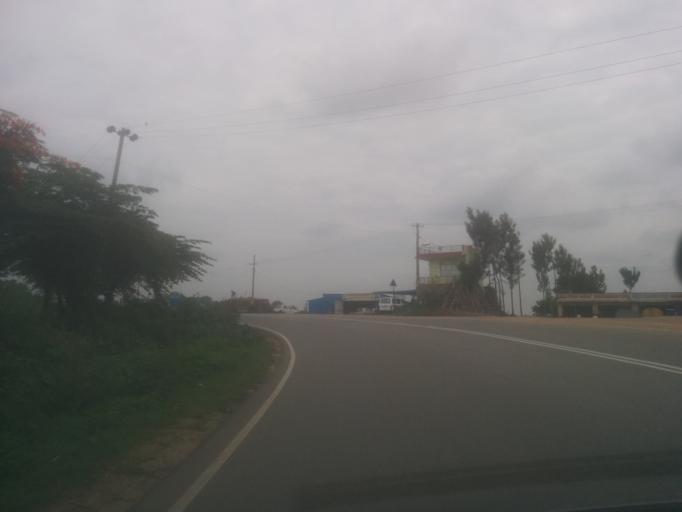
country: IN
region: Karnataka
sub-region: Hassan
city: Belur
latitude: 13.1641
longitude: 75.8819
